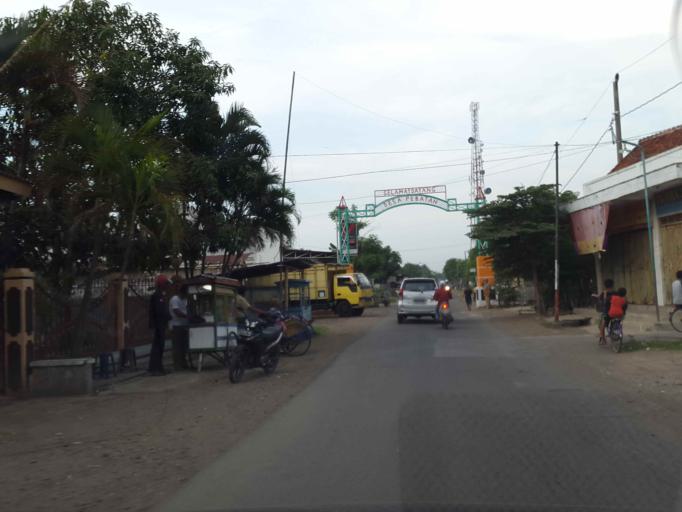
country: ID
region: Central Java
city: Dukuhturi
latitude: -6.8774
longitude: 109.0274
